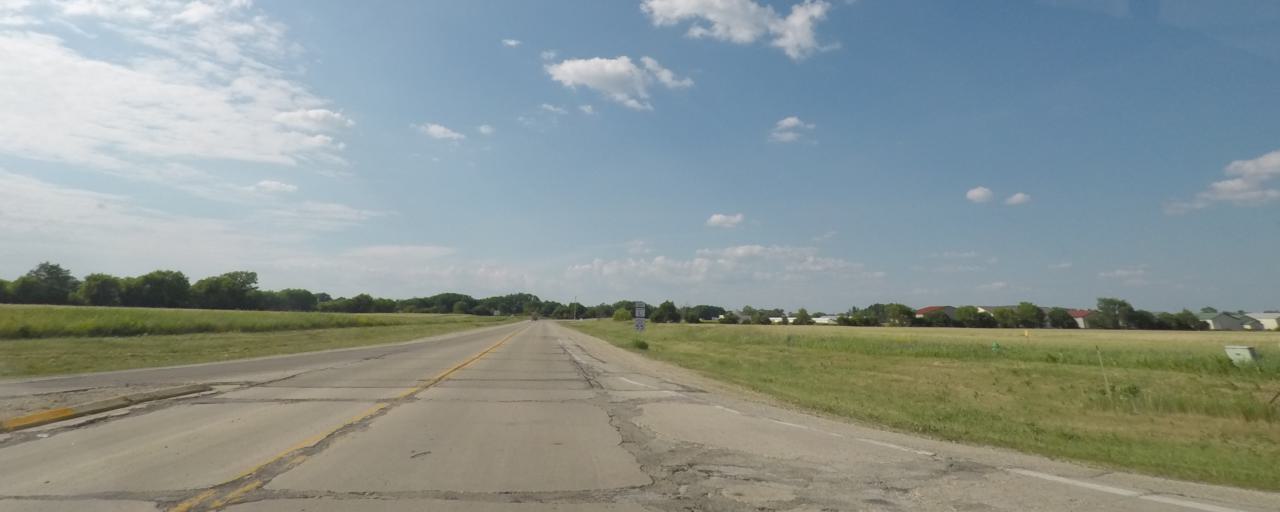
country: US
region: Wisconsin
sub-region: Walworth County
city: East Troy
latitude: 42.7924
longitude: -88.3807
